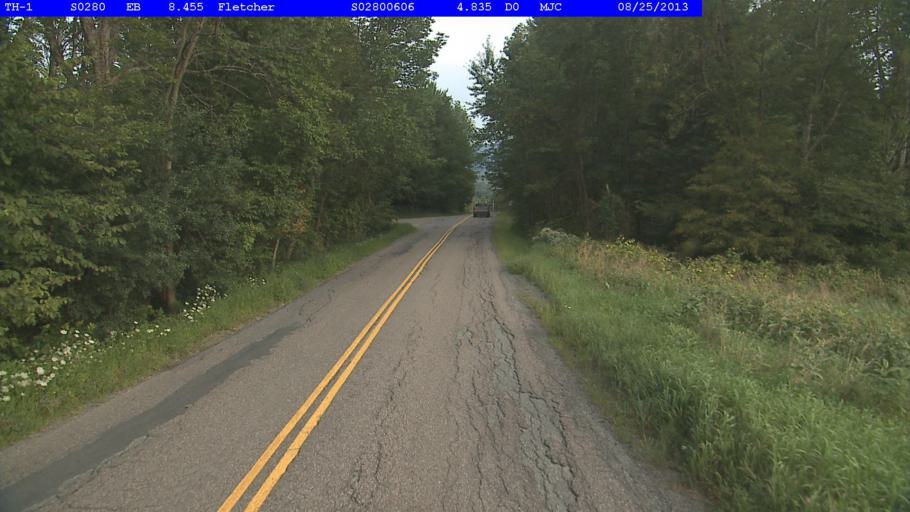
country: US
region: Vermont
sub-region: Chittenden County
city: Jericho
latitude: 44.6629
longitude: -72.8880
